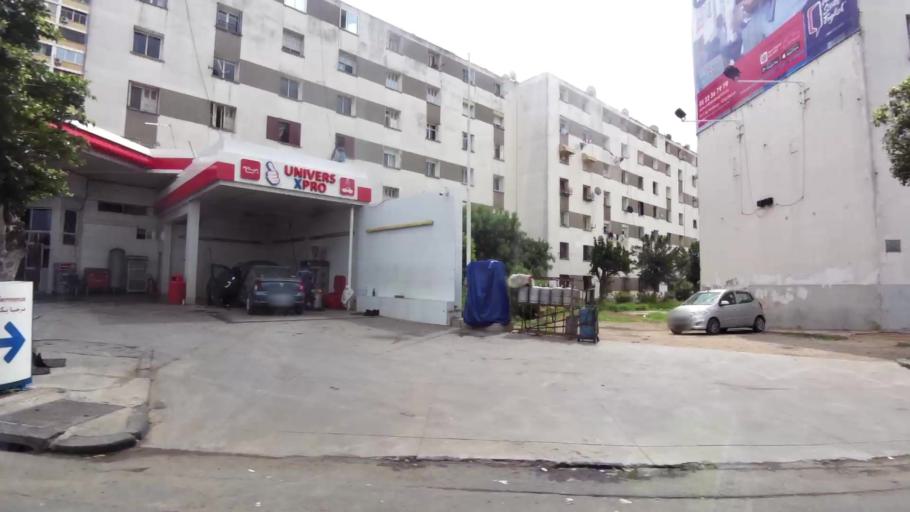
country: MA
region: Grand Casablanca
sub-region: Casablanca
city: Casablanca
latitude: 33.5860
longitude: -7.6493
